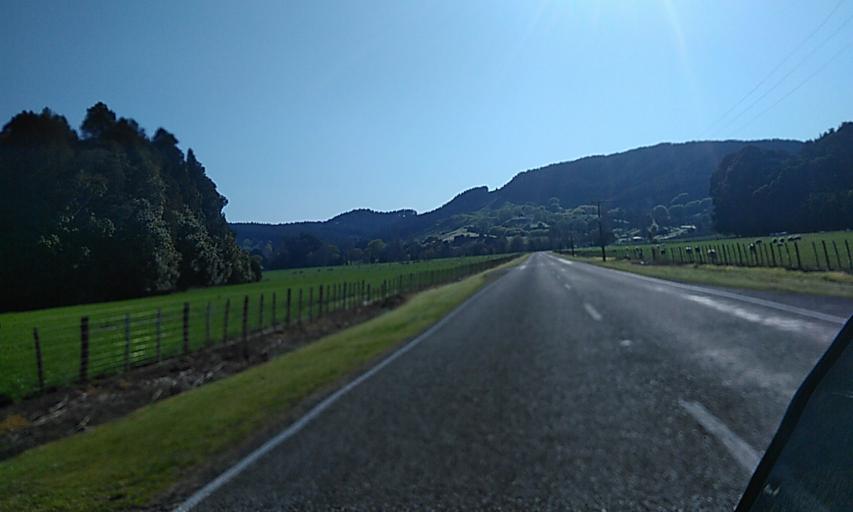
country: NZ
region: Gisborne
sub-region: Gisborne District
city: Gisborne
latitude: -38.5992
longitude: 177.9609
